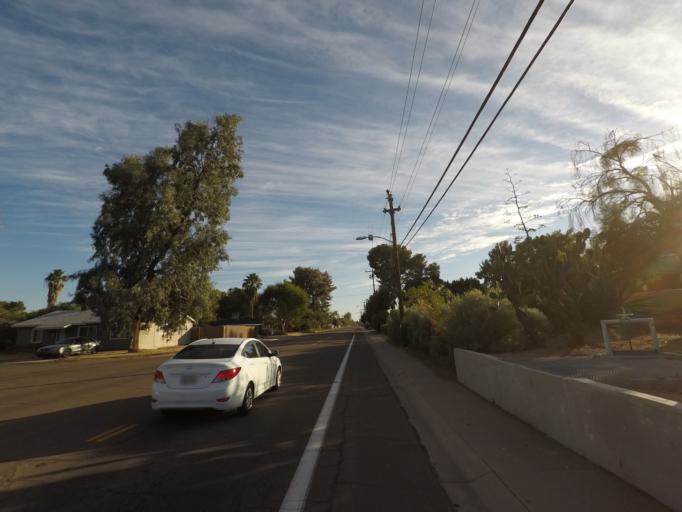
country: US
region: Arizona
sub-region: Maricopa County
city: Tempe Junction
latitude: 33.4133
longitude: -111.9479
